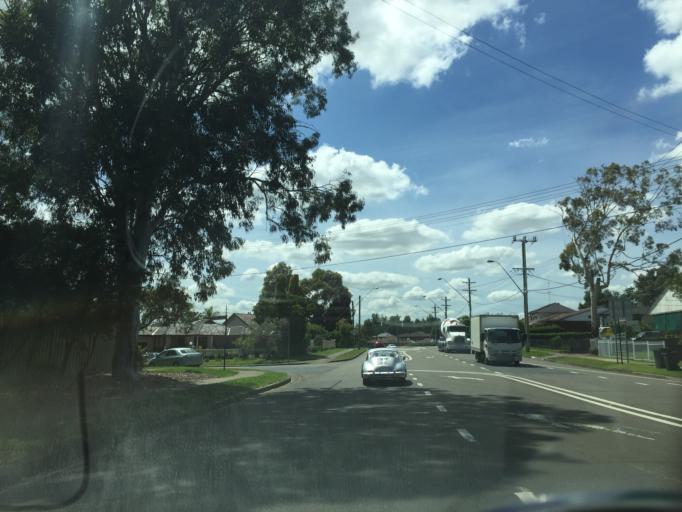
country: AU
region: New South Wales
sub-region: Parramatta
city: Constitution Hill
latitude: -33.7869
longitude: 150.9702
